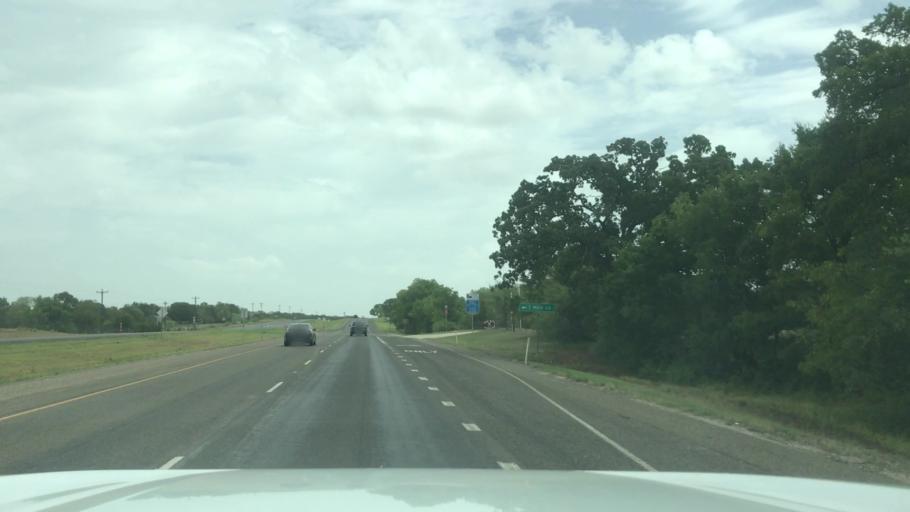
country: US
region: Texas
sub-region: McLennan County
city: Riesel
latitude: 31.5008
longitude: -96.9397
